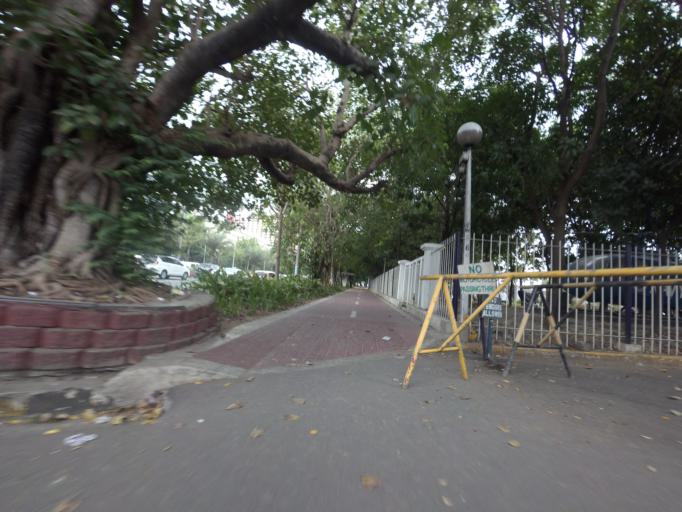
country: PH
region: Metro Manila
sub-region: City of Manila
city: Port Area
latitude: 14.5619
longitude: 120.9858
